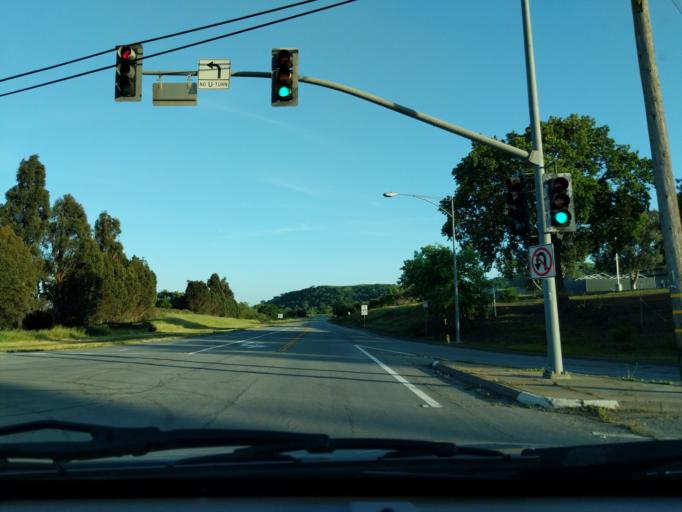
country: US
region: California
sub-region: Santa Clara County
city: Gilroy
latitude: 36.9763
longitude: -121.5683
